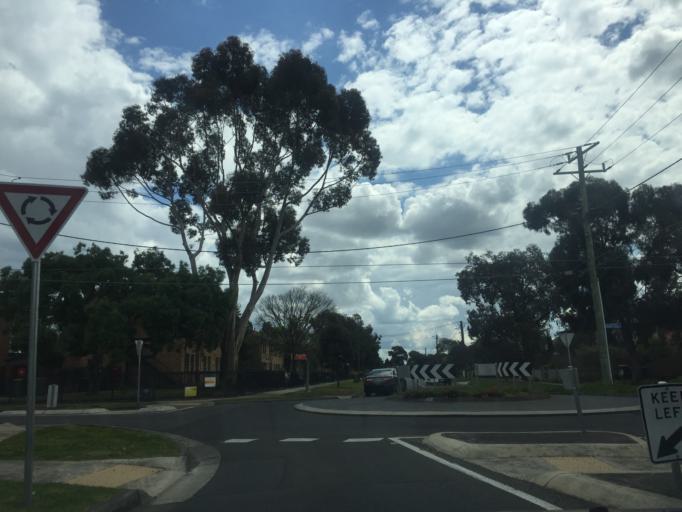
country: AU
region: Victoria
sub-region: Darebin
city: Reservoir
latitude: -37.7137
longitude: 145.0171
